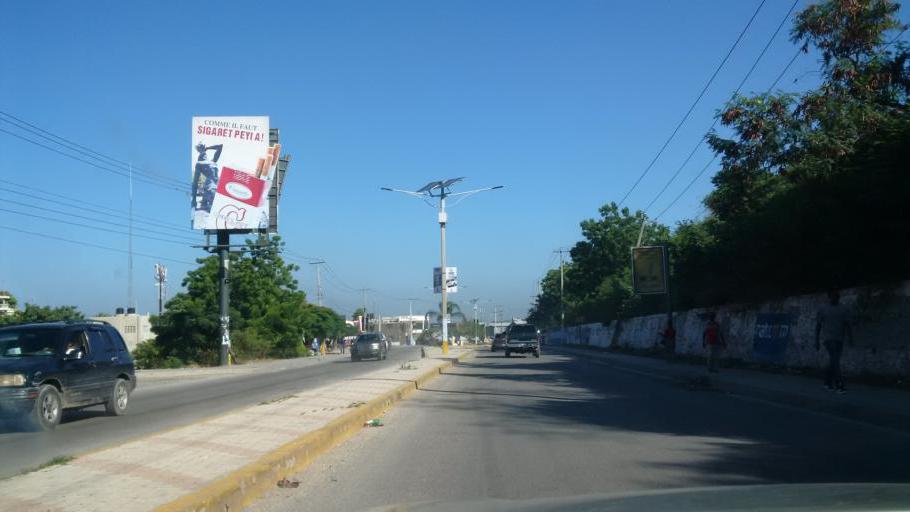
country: HT
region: Ouest
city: Delmas 73
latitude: 18.5575
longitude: -72.3173
